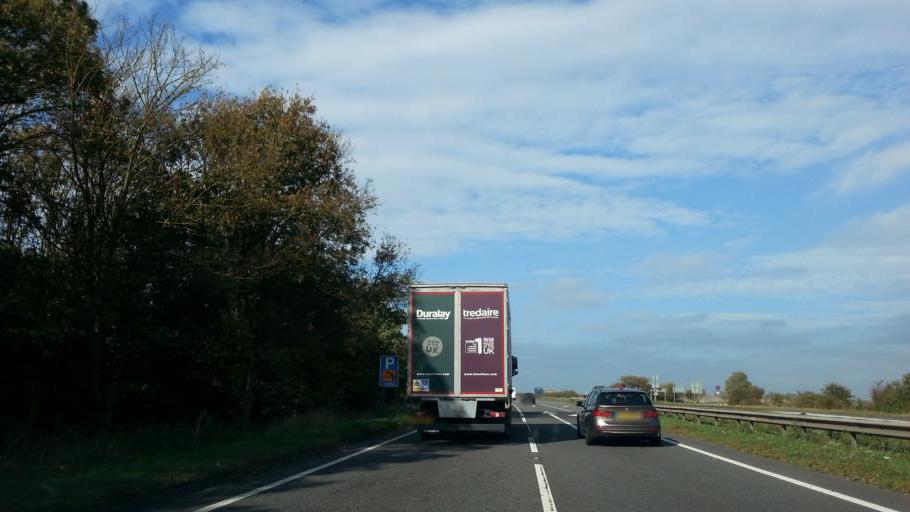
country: GB
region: England
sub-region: Lincolnshire
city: Long Bennington
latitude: 53.0289
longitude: -0.7700
